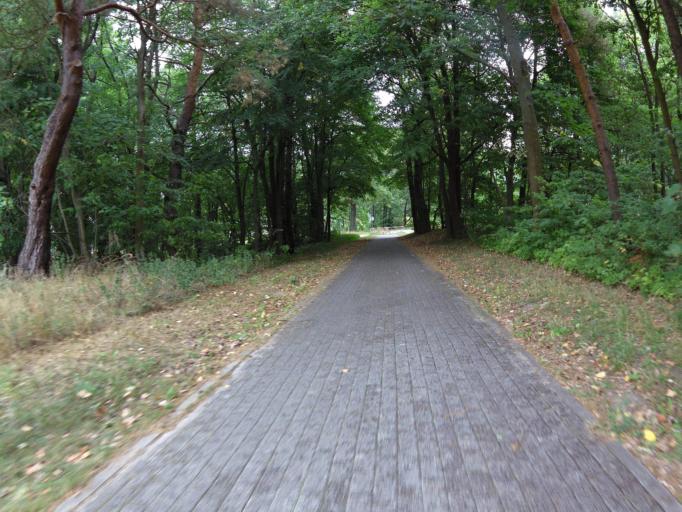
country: DE
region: Mecklenburg-Vorpommern
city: Seebad Heringsdorf
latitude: 53.8883
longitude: 14.1682
